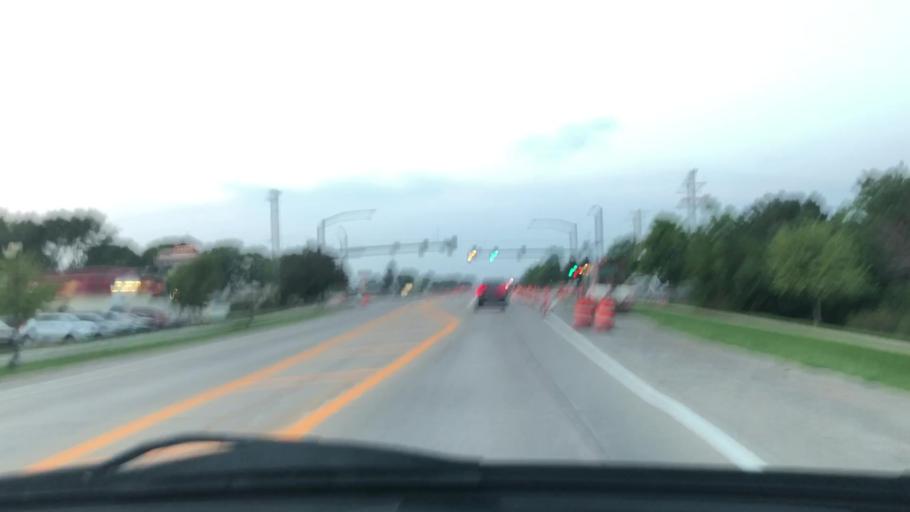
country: US
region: Iowa
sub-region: Johnson County
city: North Liberty
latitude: 41.7439
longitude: -91.6076
